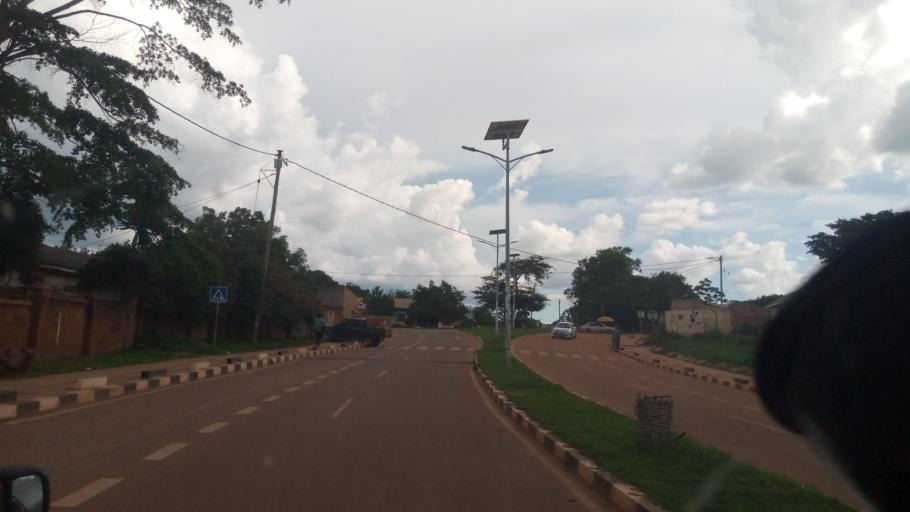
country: UG
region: Northern Region
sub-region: Lira District
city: Lira
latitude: 2.2396
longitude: 32.8997
